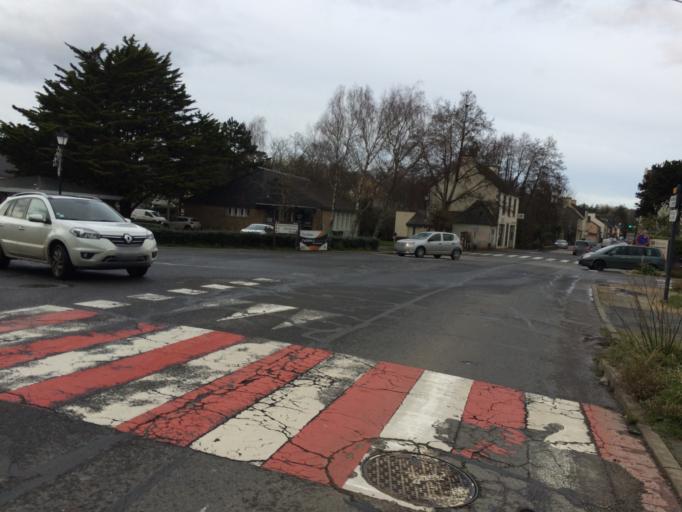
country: FR
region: Brittany
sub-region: Departement du Finistere
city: Daoulas
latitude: 48.3590
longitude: -4.2598
